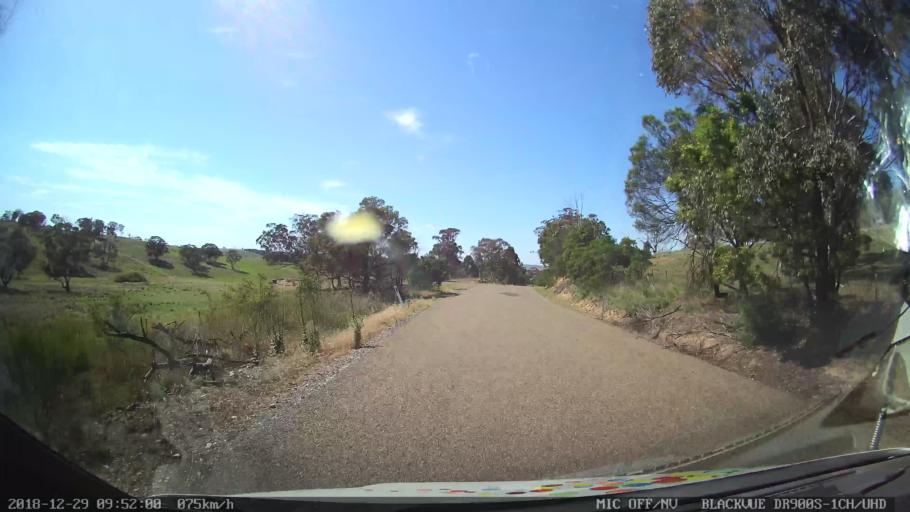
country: AU
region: New South Wales
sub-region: Goulburn Mulwaree
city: Goulburn
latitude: -34.7384
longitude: 149.4631
